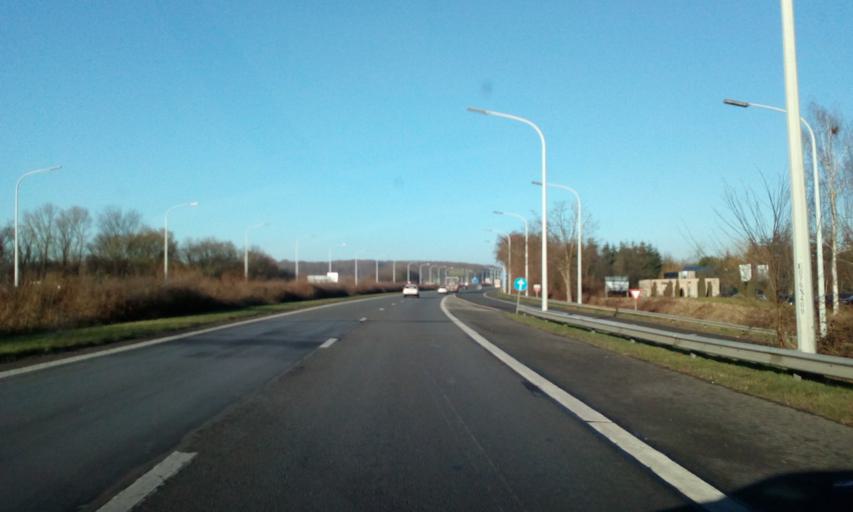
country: BE
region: Wallonia
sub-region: Province du Hainaut
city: Courcelles
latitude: 50.4649
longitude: 4.4166
